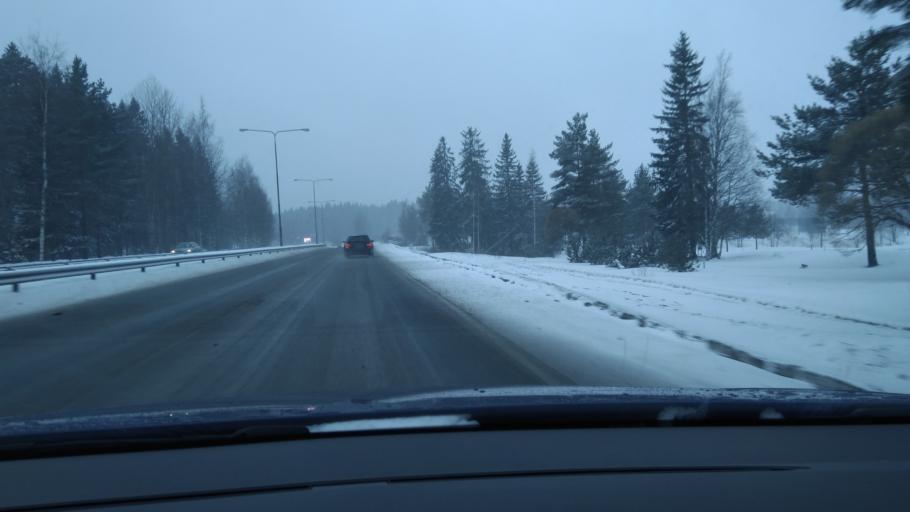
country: FI
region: Pirkanmaa
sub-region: Tampere
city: Tampere
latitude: 61.5043
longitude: 23.8530
